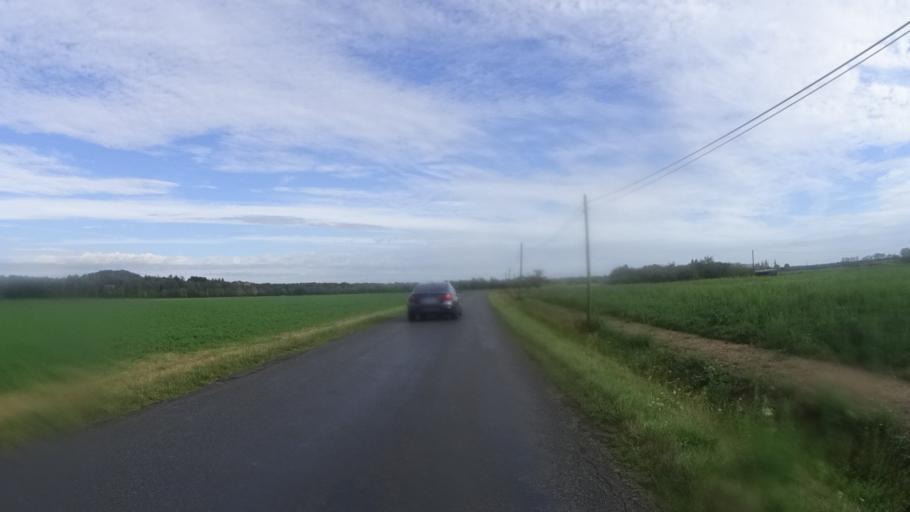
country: FR
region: Centre
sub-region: Departement du Loiret
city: Chateauneuf-sur-Loire
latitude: 47.8828
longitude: 2.2138
